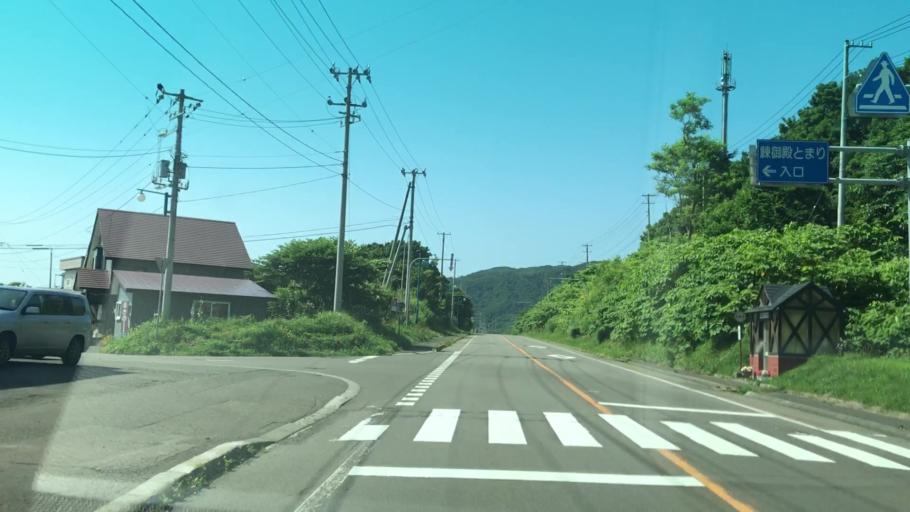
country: JP
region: Hokkaido
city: Iwanai
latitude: 43.0682
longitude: 140.4937
